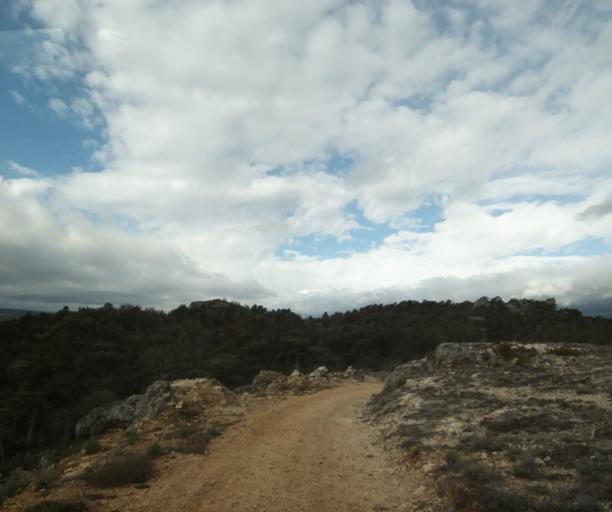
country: FR
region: Midi-Pyrenees
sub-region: Departement de l'Aveyron
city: Millau
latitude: 44.1153
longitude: 3.1514
